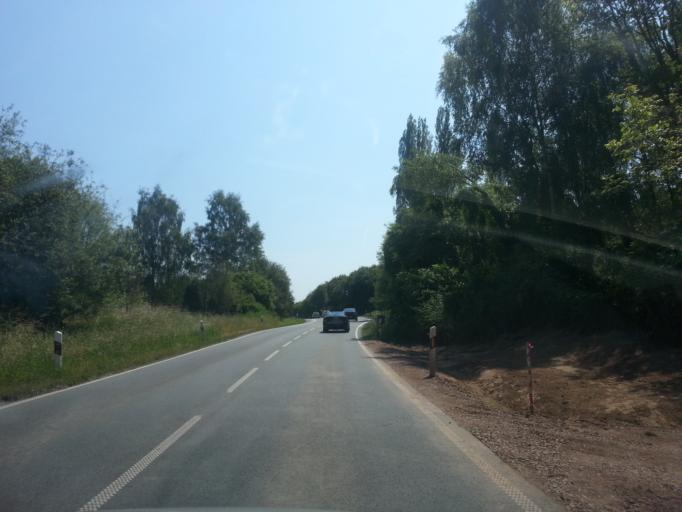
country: DE
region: Hesse
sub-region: Regierungsbezirk Darmstadt
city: Dietzenbach
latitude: 50.0026
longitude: 8.7603
